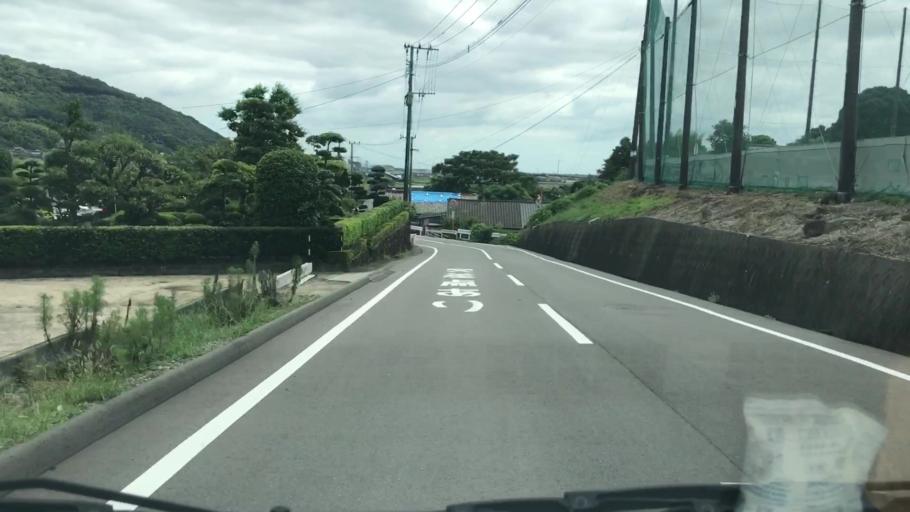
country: JP
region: Saga Prefecture
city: Takeocho-takeo
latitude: 33.2319
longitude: 130.1434
